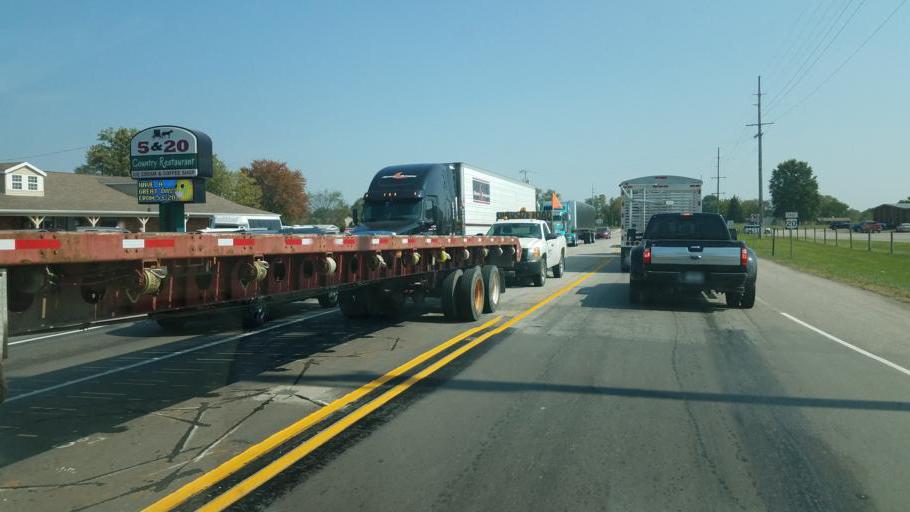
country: US
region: Indiana
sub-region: LaGrange County
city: Topeka
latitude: 41.6546
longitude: -85.5801
